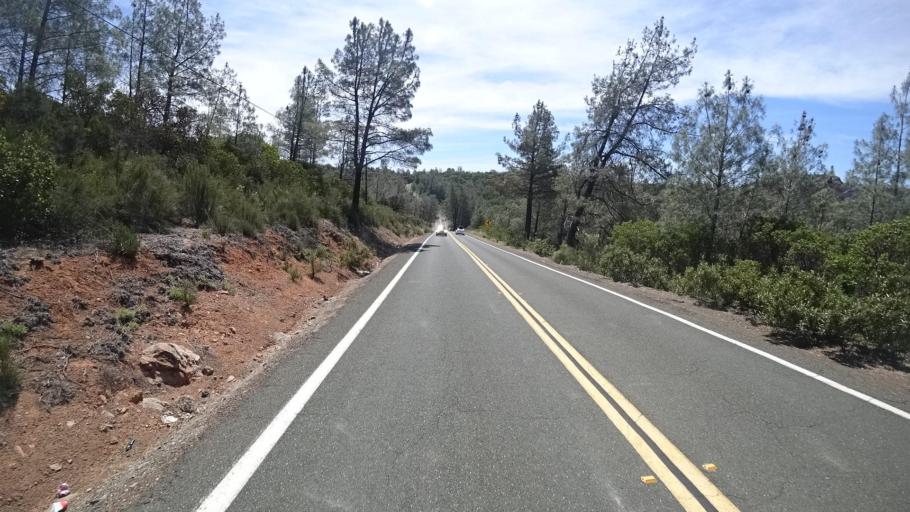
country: US
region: California
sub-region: Lake County
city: Clearlake
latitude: 38.9339
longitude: -122.6615
